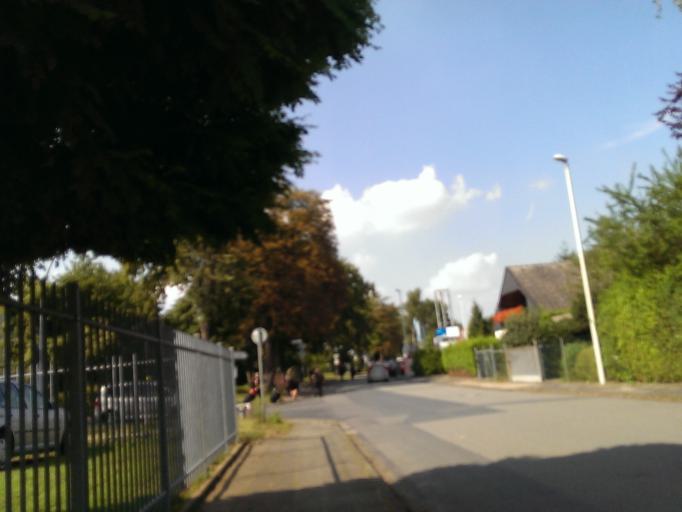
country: DE
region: Lower Saxony
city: Hildesheim
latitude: 52.1748
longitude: 9.9526
